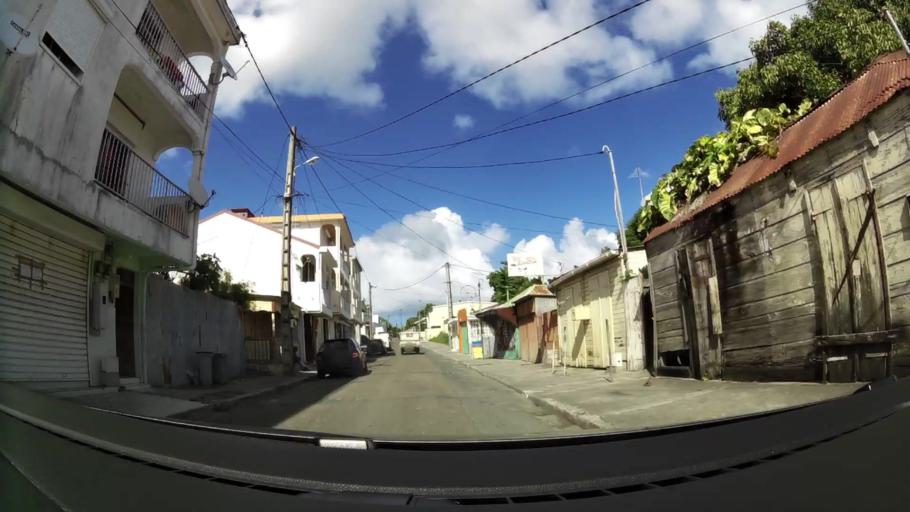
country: GP
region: Guadeloupe
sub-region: Guadeloupe
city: Saint-Francois
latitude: 16.2524
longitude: -61.2722
